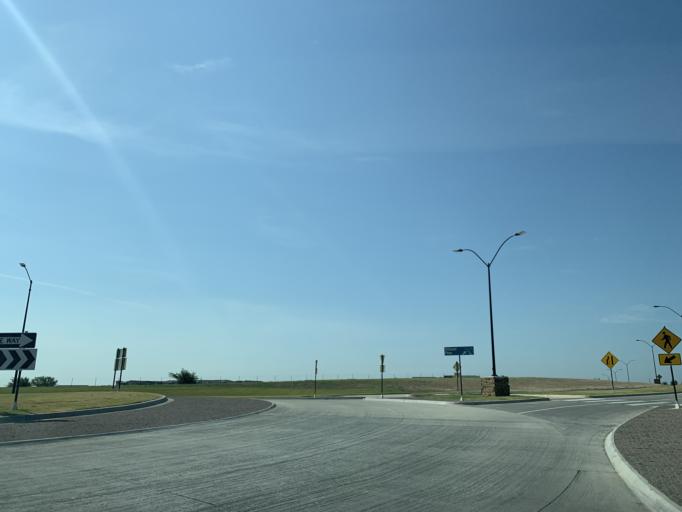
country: US
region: Texas
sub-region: Tarrant County
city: Keller
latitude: 32.9235
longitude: -97.3123
